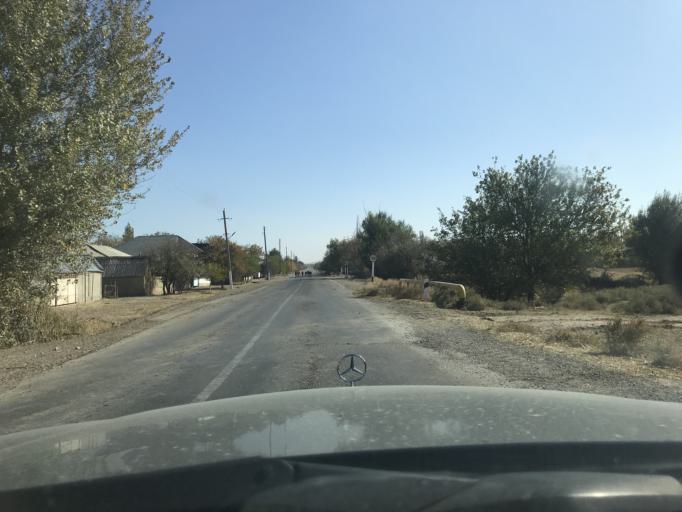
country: KZ
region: Ongtustik Qazaqstan
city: Sastobe
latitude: 42.5464
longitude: 69.9199
